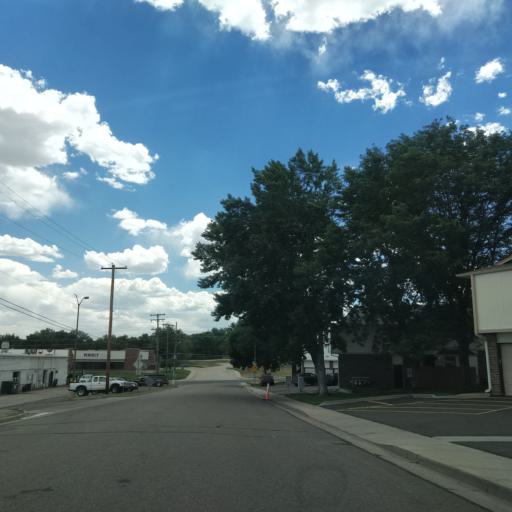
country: US
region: Colorado
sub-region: Jefferson County
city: Lakewood
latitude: 39.6833
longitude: -105.0862
